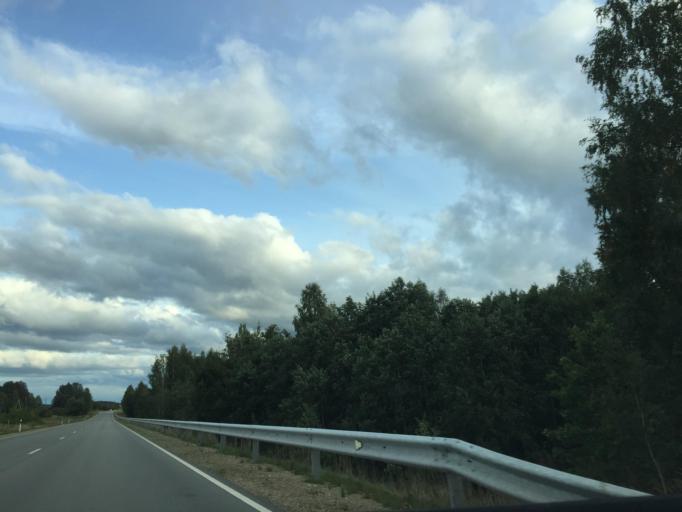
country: LV
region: Nereta
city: Nereta
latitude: 56.2426
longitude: 25.2596
